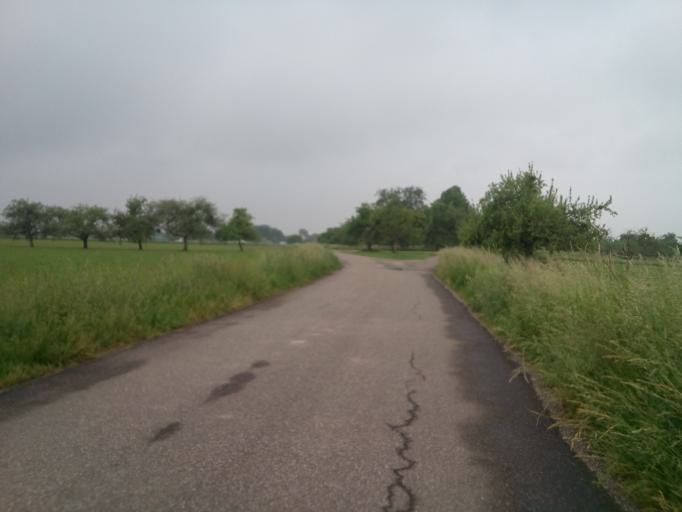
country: DE
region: Baden-Wuerttemberg
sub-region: Freiburg Region
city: Rheinau
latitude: 48.6781
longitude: 7.9507
